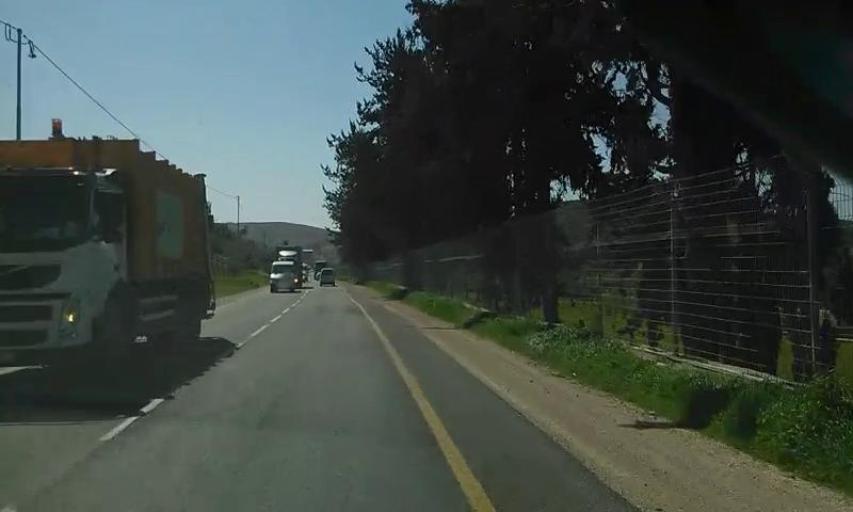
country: PS
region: West Bank
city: Shuyukh al `Arrub
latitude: 31.6304
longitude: 35.1322
